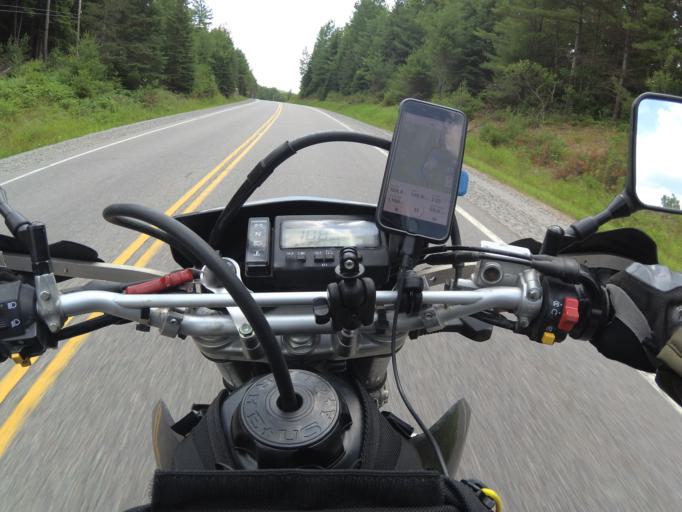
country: CA
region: Ontario
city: Bancroft
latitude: 45.0168
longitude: -77.2729
